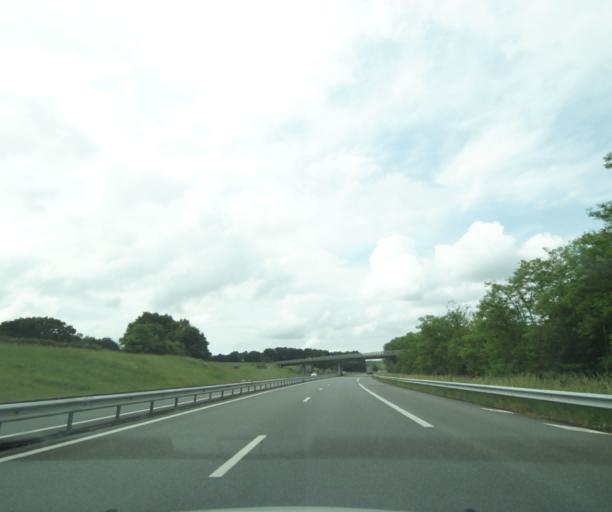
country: FR
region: Centre
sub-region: Departement du Cher
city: Orval
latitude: 46.7297
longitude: 2.4306
